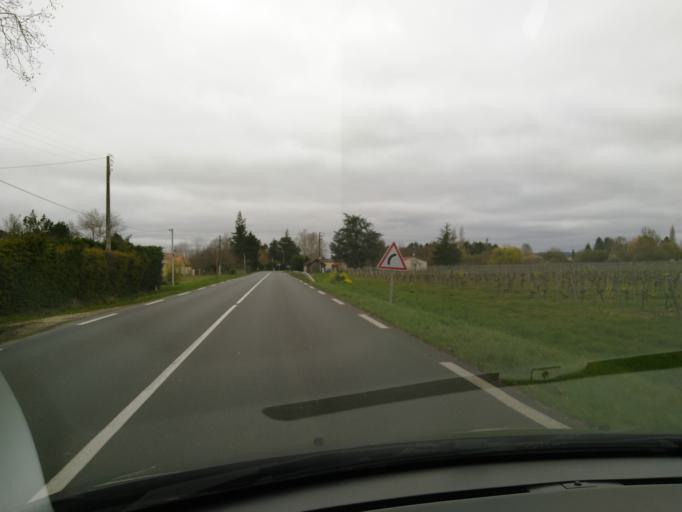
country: FR
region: Aquitaine
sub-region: Departement de la Dordogne
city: Monbazillac
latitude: 44.8133
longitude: 0.5075
